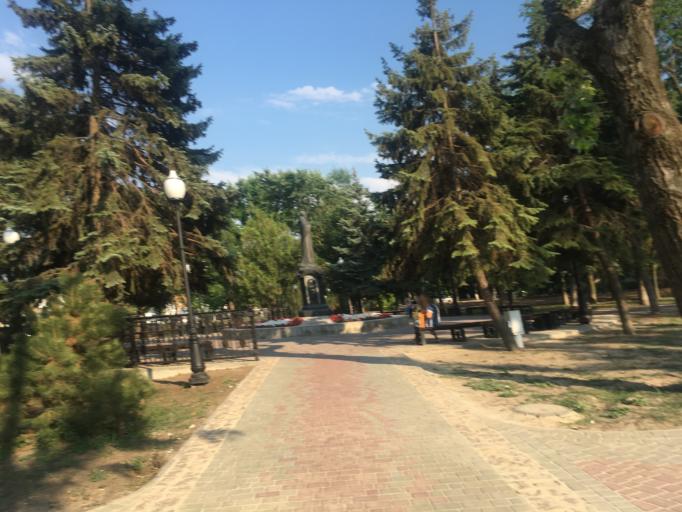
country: RU
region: Krasnodarskiy
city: Yeysk
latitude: 46.7141
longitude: 38.2751
